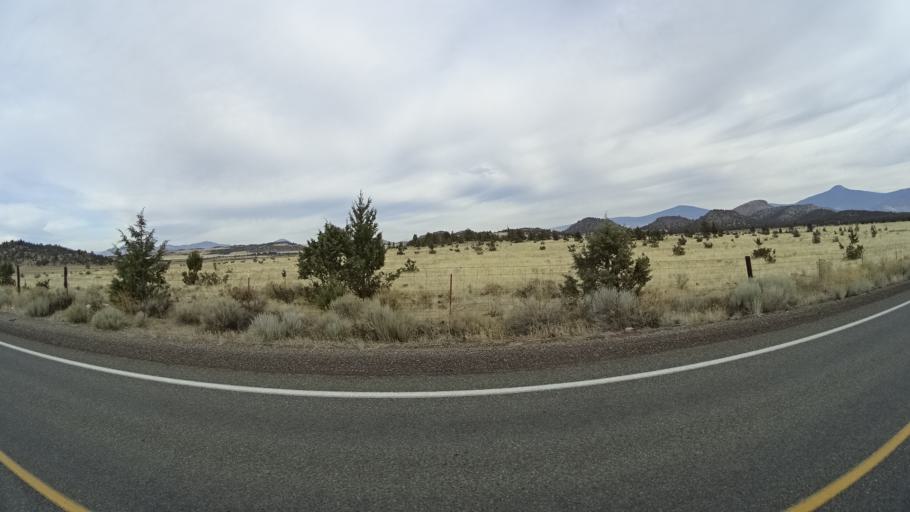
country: US
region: California
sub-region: Siskiyou County
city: Montague
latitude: 41.6402
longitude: -122.4699
